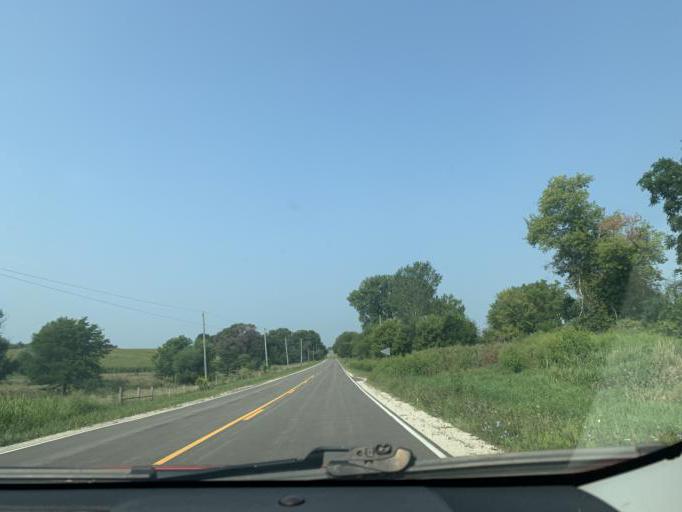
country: US
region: Illinois
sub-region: Whiteside County
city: Sterling
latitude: 41.8442
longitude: -89.7896
